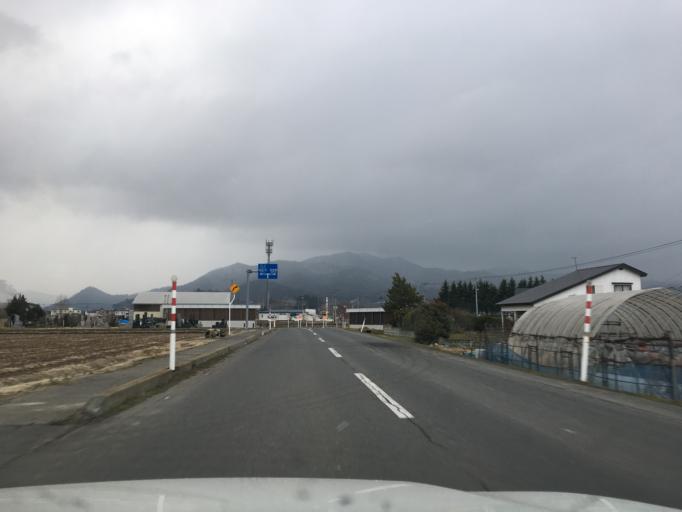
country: JP
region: Aomori
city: Hirosaki
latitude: 40.5580
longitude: 140.5466
